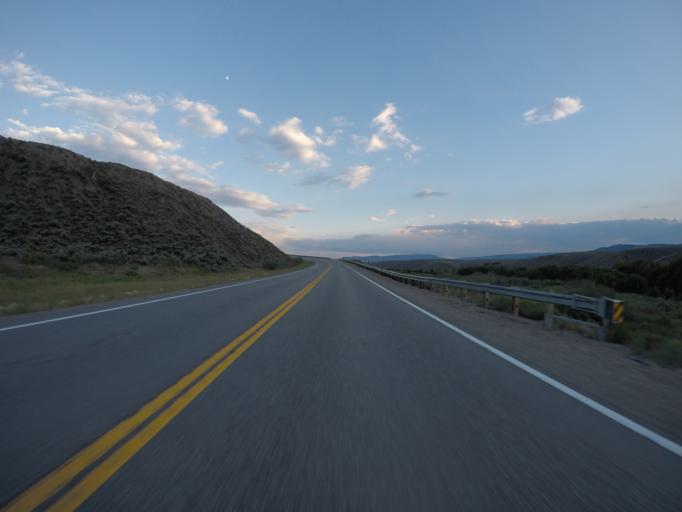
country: US
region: Colorado
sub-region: Grand County
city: Kremmling
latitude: 40.2289
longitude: -106.4365
